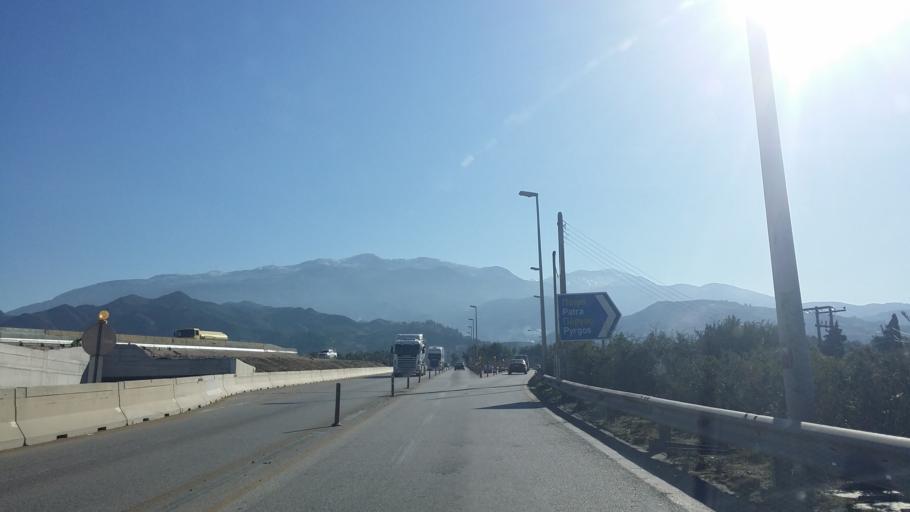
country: GR
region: West Greece
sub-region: Nomos Achaias
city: Rio
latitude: 38.3012
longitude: 21.7900
